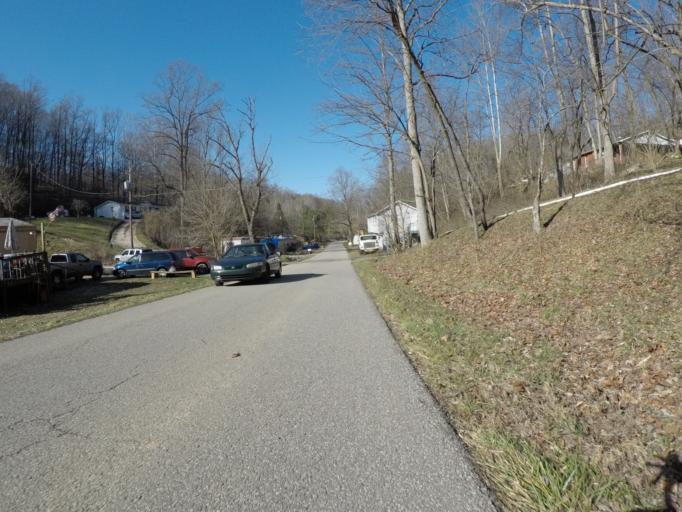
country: US
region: Kentucky
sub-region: Boyd County
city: Catlettsburg
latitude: 38.4055
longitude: -82.6365
